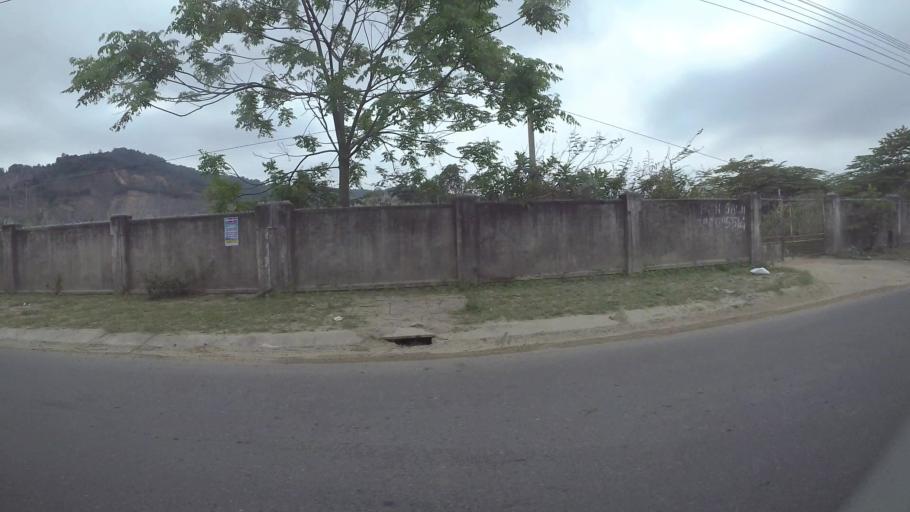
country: VN
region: Da Nang
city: Lien Chieu
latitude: 16.0469
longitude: 108.1641
